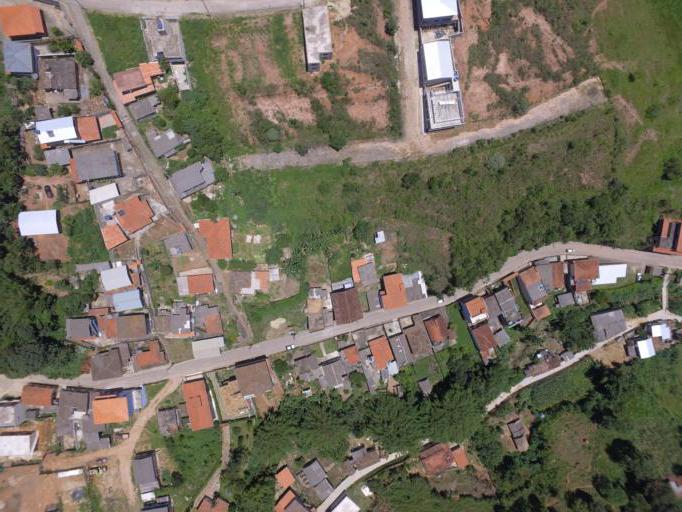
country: BR
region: Minas Gerais
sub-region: Tiradentes
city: Tiradentes
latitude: -21.0627
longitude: -44.0797
